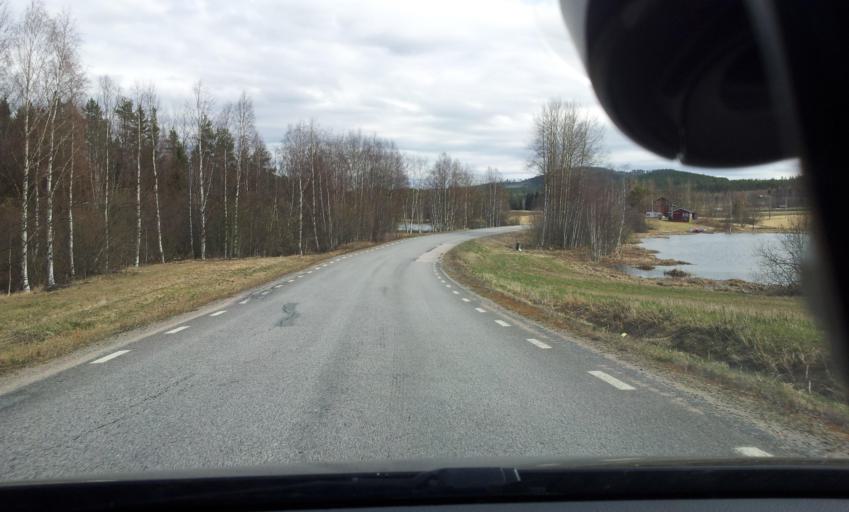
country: SE
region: Gaevleborg
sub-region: Ljusdals Kommun
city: Farila
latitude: 61.7724
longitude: 15.9614
